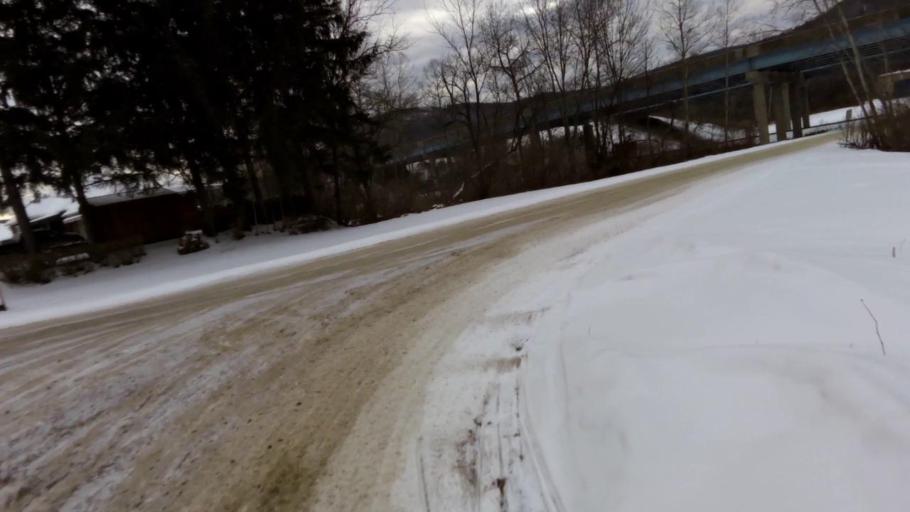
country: US
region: Pennsylvania
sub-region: McKean County
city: Foster Brook
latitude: 41.9991
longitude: -78.6179
